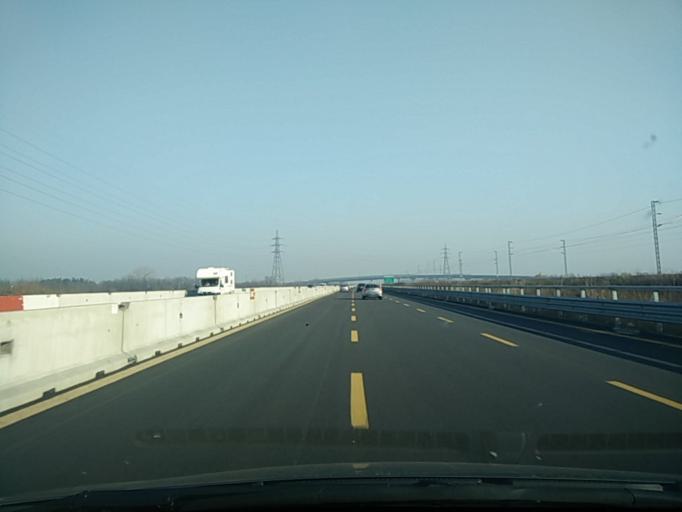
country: IT
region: Lombardy
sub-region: Citta metropolitana di Milano
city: Casone
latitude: 45.4943
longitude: 8.8886
